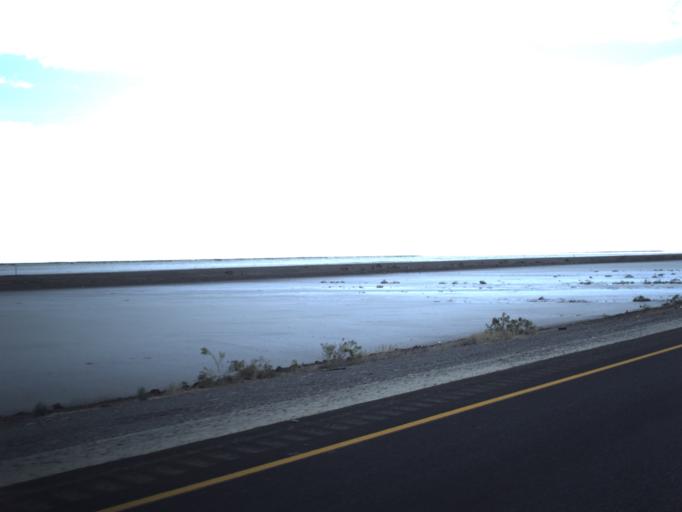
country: US
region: Utah
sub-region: Tooele County
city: Wendover
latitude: 40.7317
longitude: -113.5367
